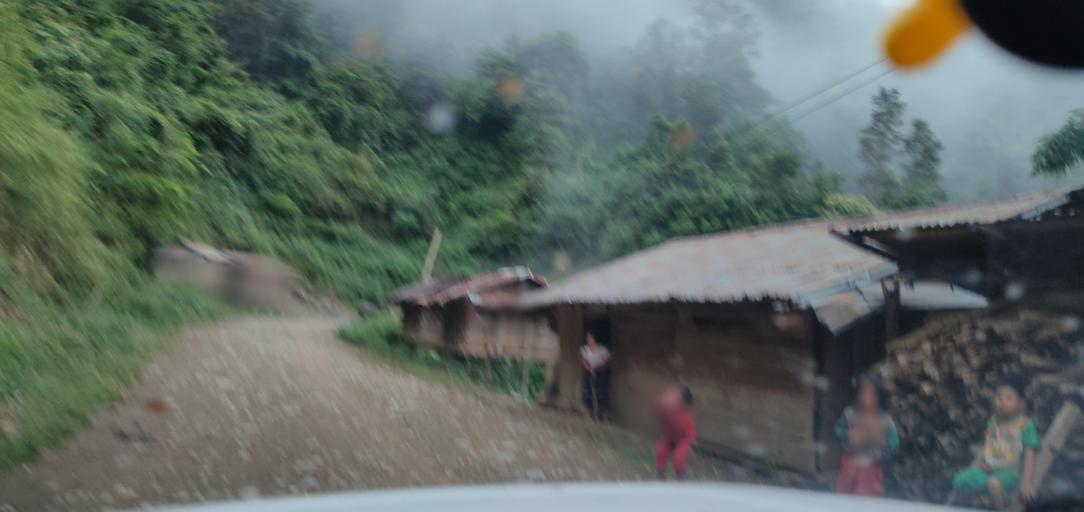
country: LA
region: Phongsali
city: Phongsali
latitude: 21.4443
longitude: 102.2972
